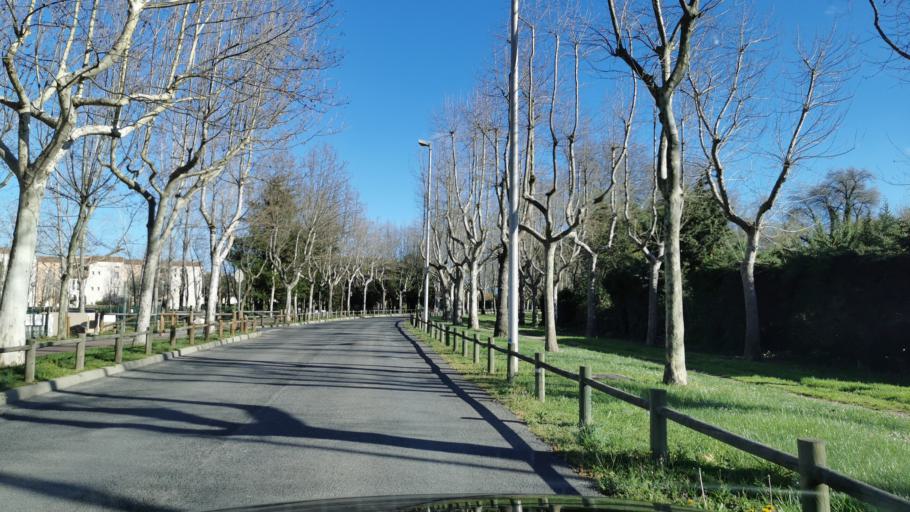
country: FR
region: Languedoc-Roussillon
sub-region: Departement des Pyrenees-Orientales
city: Saint-Cyprien-Plage
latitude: 42.6083
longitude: 3.0329
